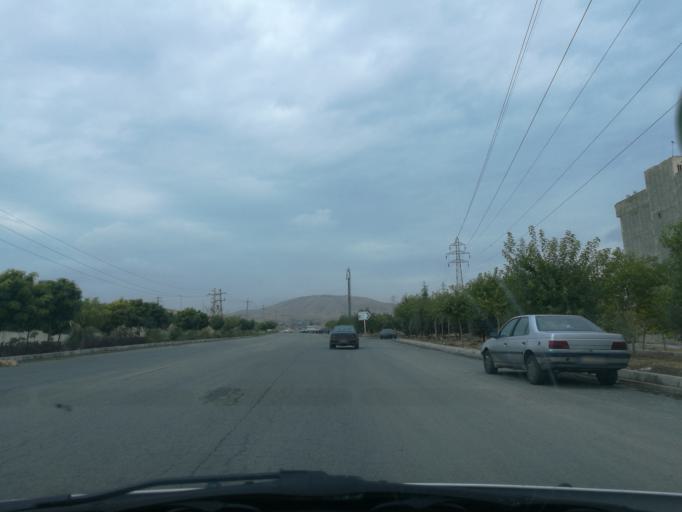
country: IR
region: Alborz
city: Karaj
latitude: 35.8639
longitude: 50.9267
